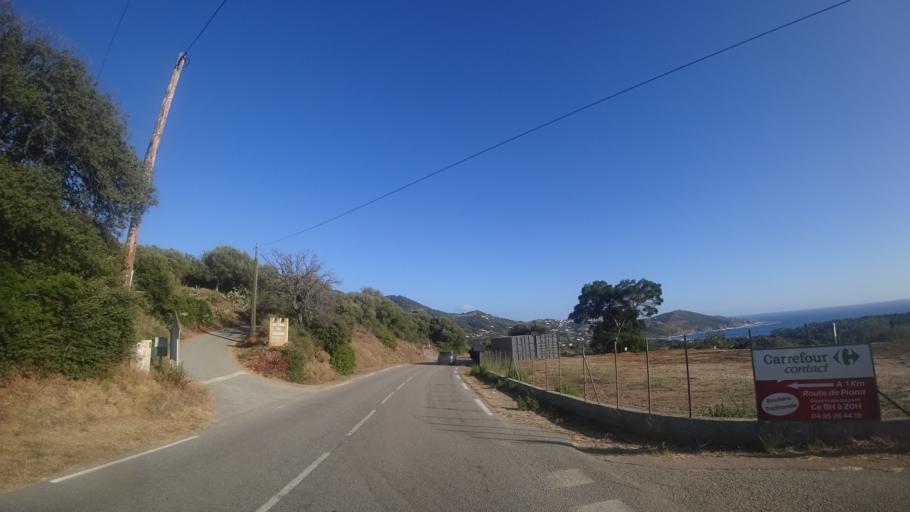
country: FR
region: Corsica
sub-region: Departement de la Corse-du-Sud
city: Cargese
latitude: 42.1608
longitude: 8.5969
